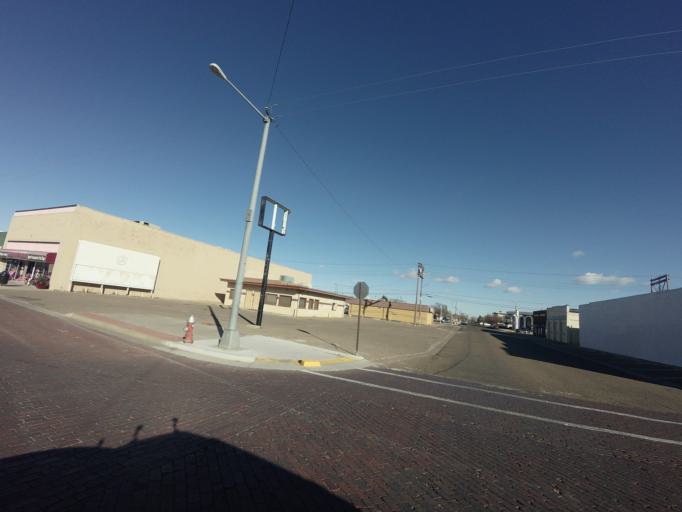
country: US
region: New Mexico
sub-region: Curry County
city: Clovis
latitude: 34.4029
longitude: -103.2053
